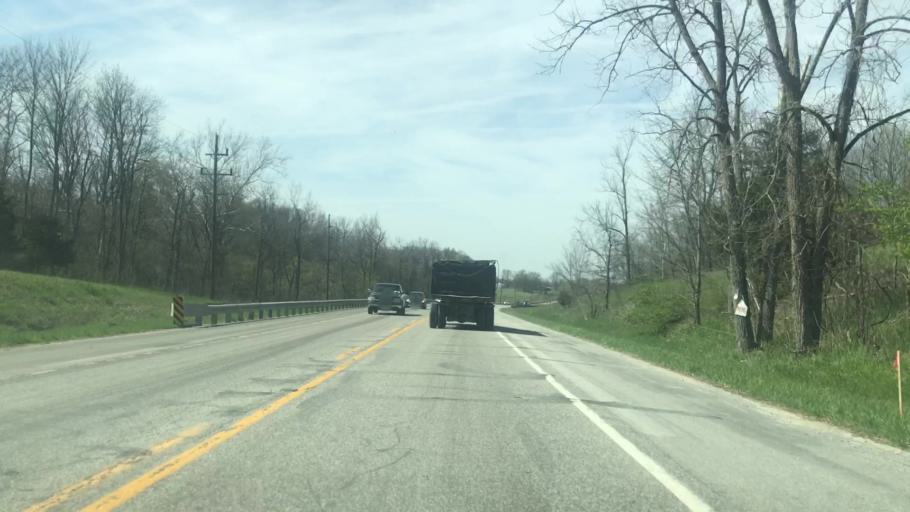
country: US
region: Indiana
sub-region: Putnam County
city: Cloverdale
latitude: 39.5504
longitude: -86.8093
